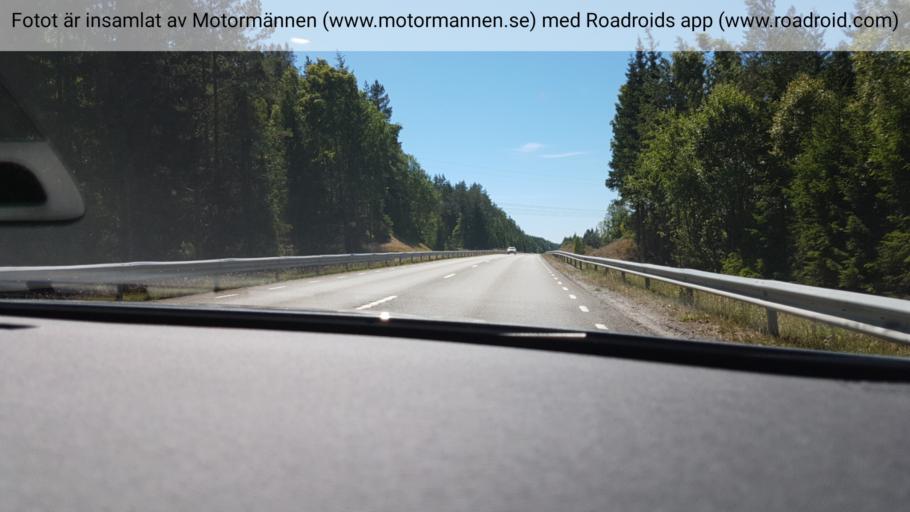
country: SE
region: Joenkoeping
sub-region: Gnosjo Kommun
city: Marieholm
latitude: 57.6118
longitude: 13.7617
